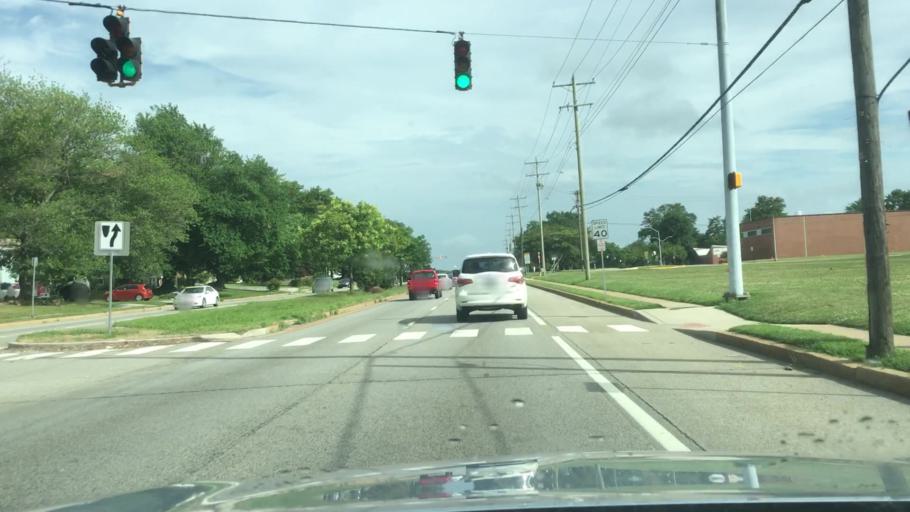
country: US
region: Delaware
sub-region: New Castle County
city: Newport
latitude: 39.7163
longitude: -75.6516
